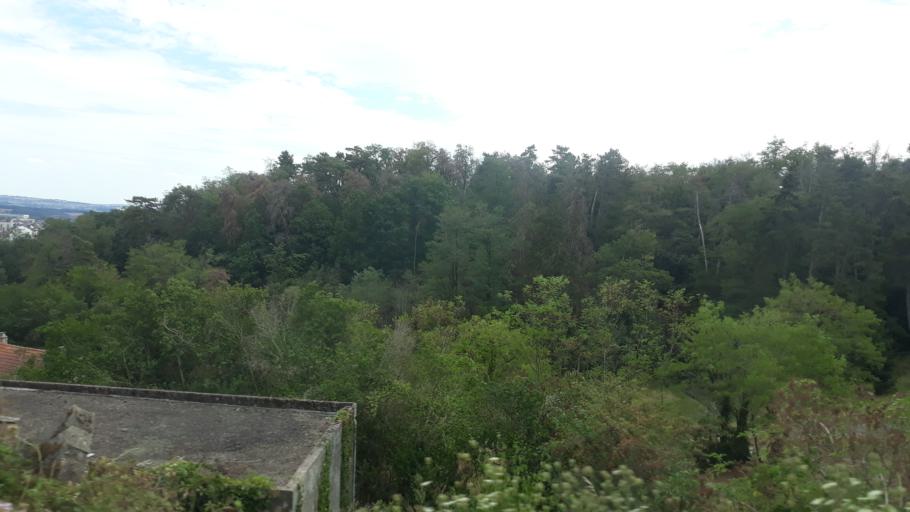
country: FR
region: Bourgogne
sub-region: Departement de Saone-et-Loire
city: Le Creusot
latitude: 46.8140
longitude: 4.4200
